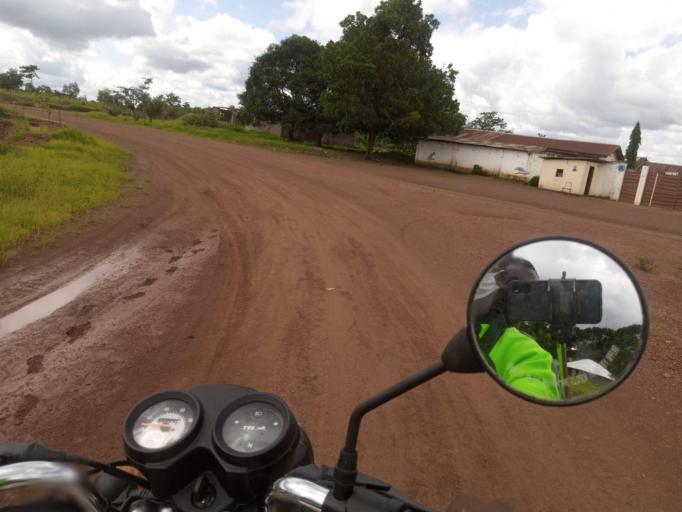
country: SL
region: Northern Province
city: Port Loko
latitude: 8.7690
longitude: -12.7742
